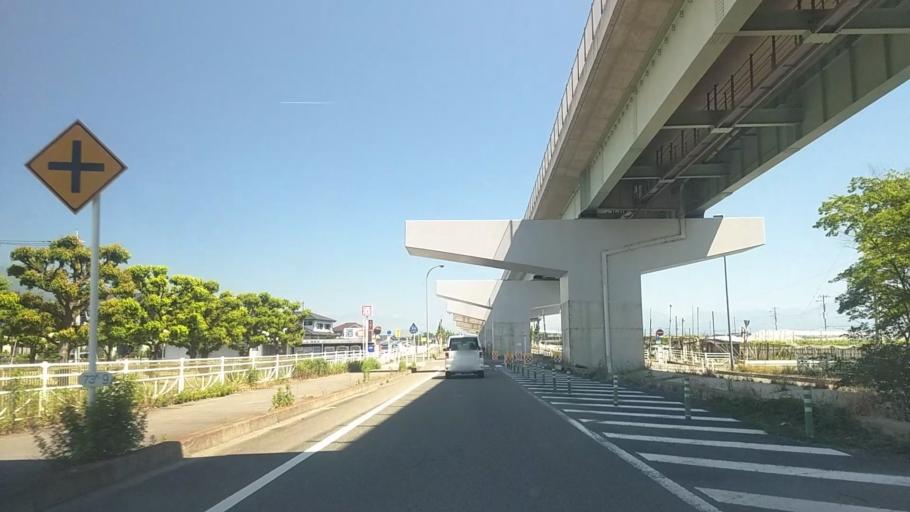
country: JP
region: Yamanashi
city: Ryuo
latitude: 35.5830
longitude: 138.4748
